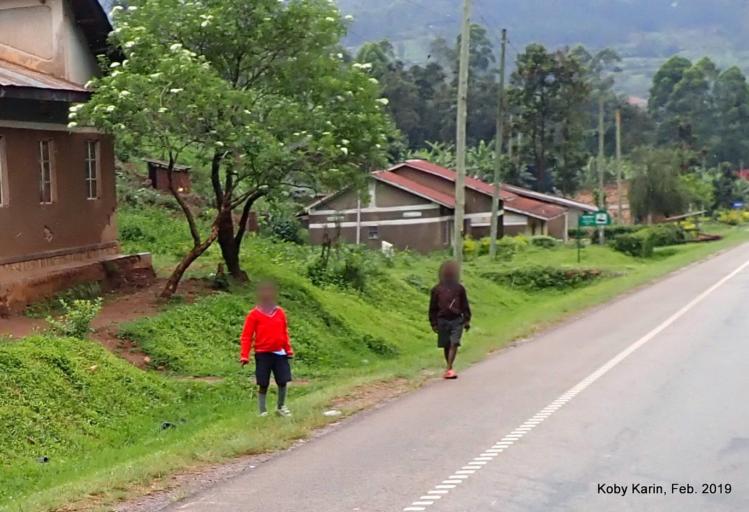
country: UG
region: Western Region
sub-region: Kabale District
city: Kabale
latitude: -1.1667
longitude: 30.1324
